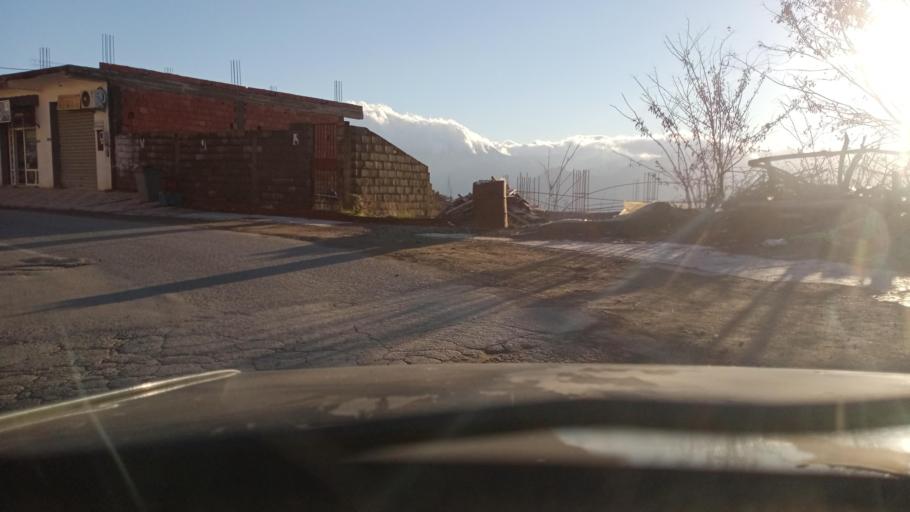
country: DZ
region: Tizi Ouzou
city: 'Ain el Hammam
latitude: 36.5631
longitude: 4.3235
